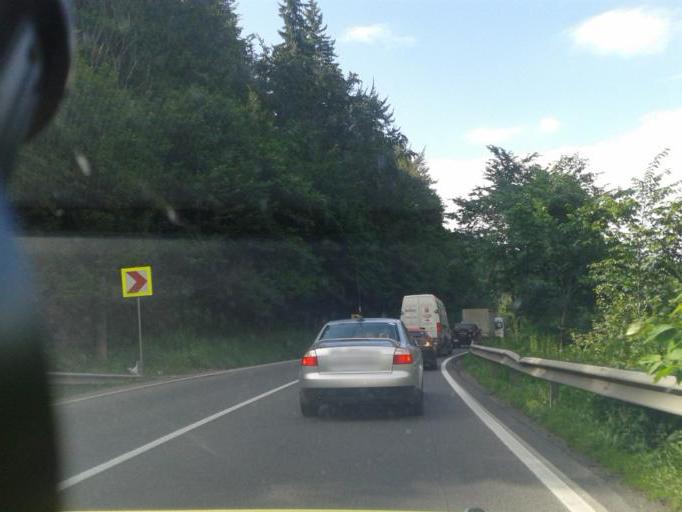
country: RO
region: Prahova
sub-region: Oras Busteni
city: Poiana Tapului
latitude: 45.3819
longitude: 25.5379
